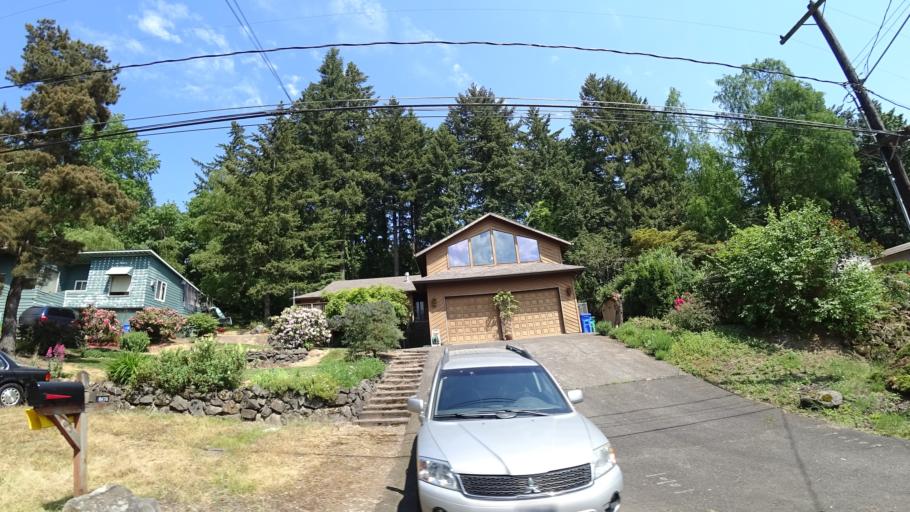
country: US
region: Oregon
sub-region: Washington County
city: Metzger
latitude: 45.4497
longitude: -122.7334
